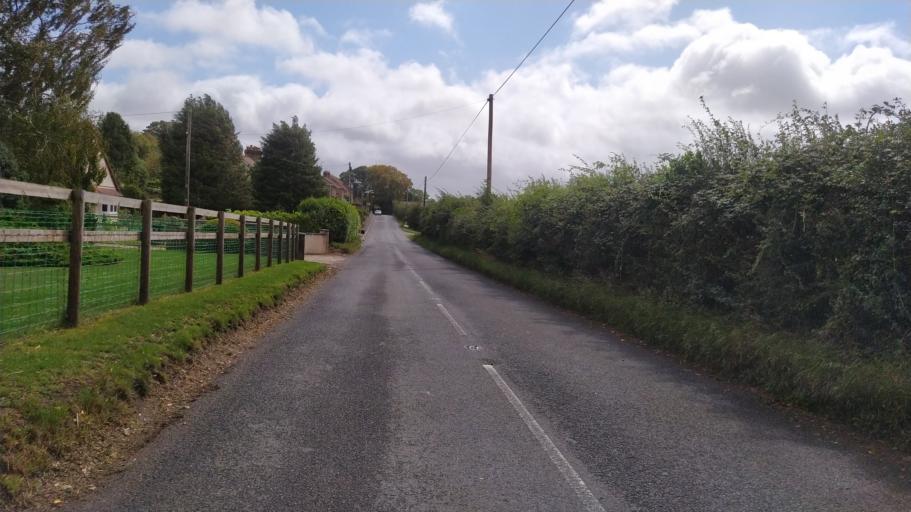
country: GB
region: England
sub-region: Wiltshire
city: Bower Chalke
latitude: 50.9553
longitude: -2.0122
